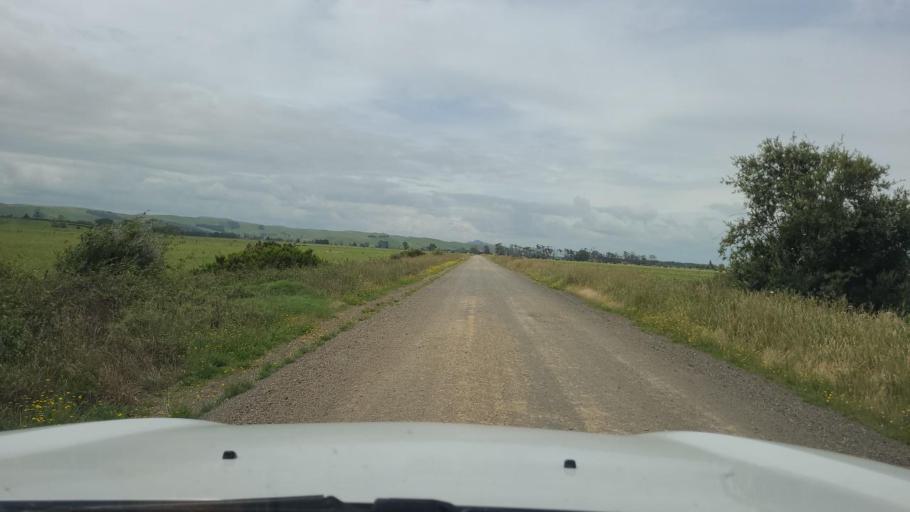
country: NZ
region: Waikato
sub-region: Hamilton City
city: Hamilton
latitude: -37.6767
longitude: 175.4421
